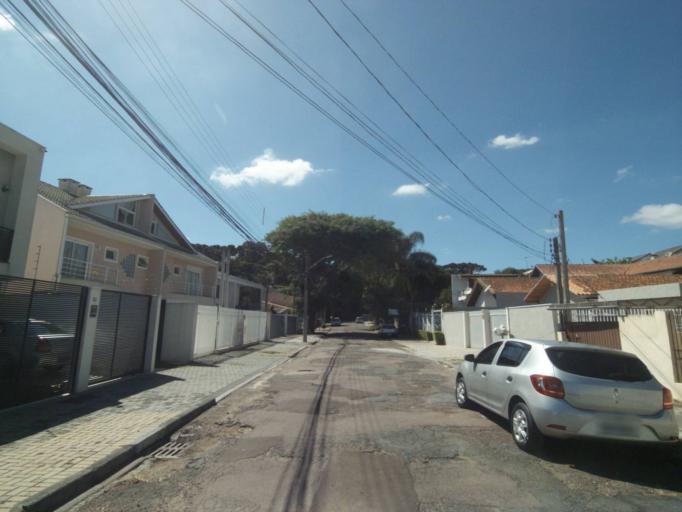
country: BR
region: Parana
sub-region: Pinhais
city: Pinhais
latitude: -25.4358
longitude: -49.2218
